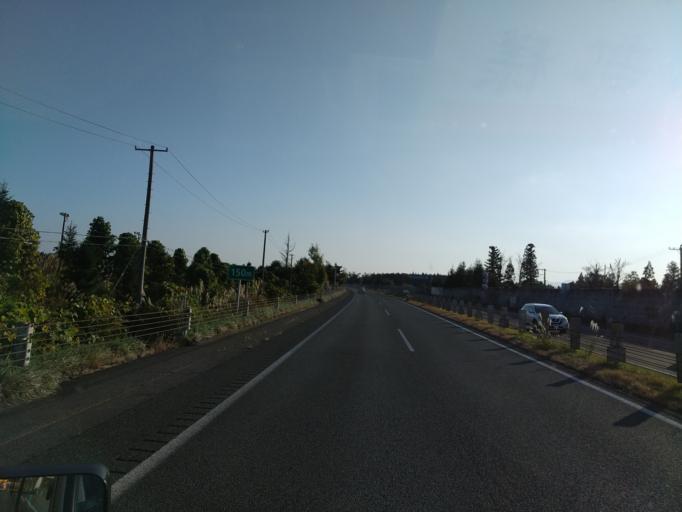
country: JP
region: Iwate
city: Hanamaki
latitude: 39.4087
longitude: 141.0934
